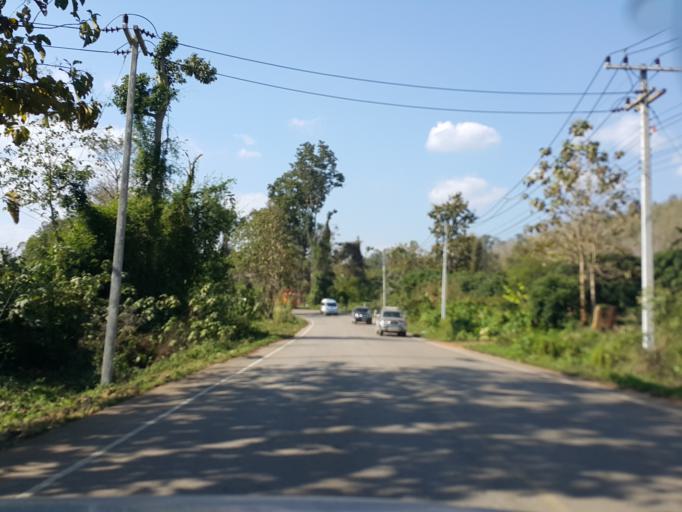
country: TH
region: Chiang Mai
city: Mae Wang
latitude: 18.6440
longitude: 98.6987
